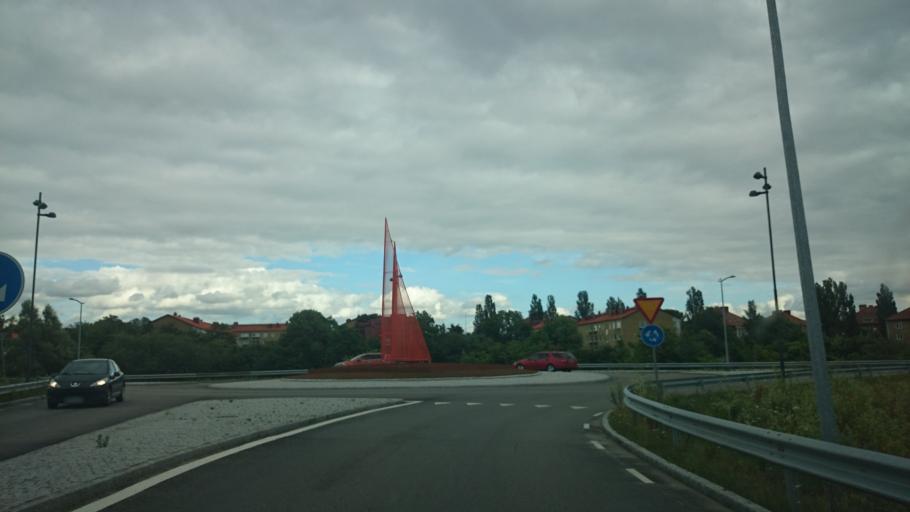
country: SE
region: Skane
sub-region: Lomma Kommun
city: Lomma
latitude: 55.6803
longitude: 13.0724
